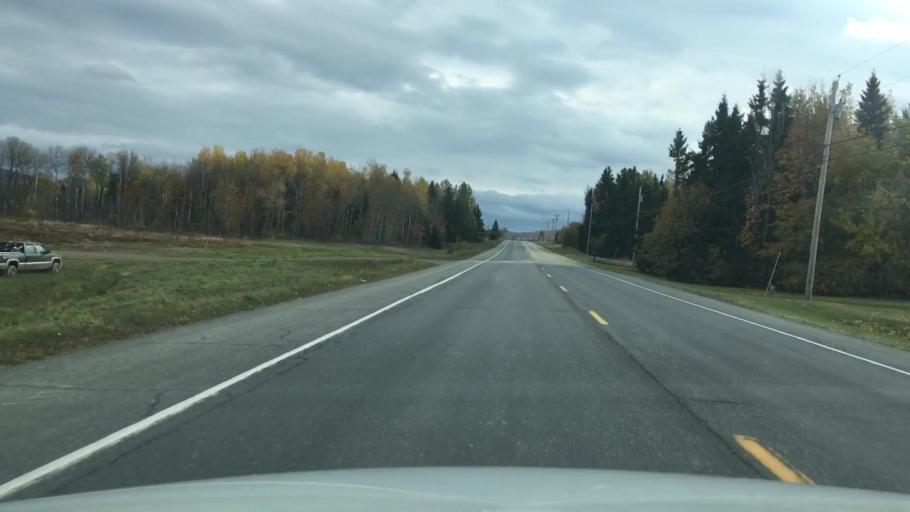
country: US
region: Maine
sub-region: Aroostook County
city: Easton
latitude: 46.5615
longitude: -67.9446
